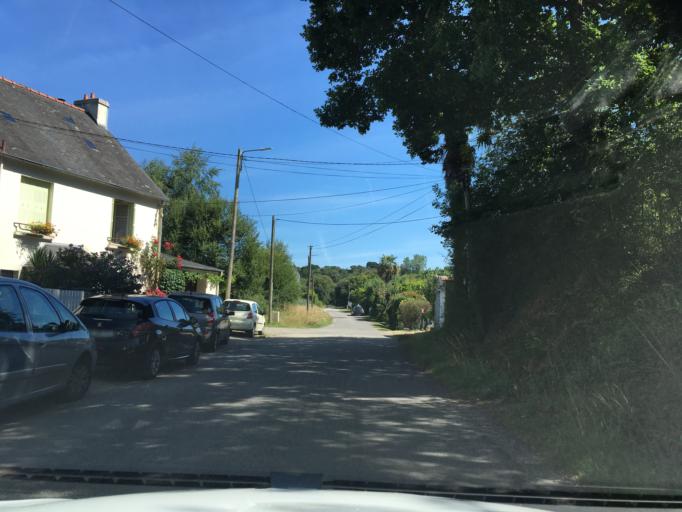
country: FR
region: Brittany
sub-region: Departement du Finistere
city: Quimper
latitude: 47.9767
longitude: -4.1193
